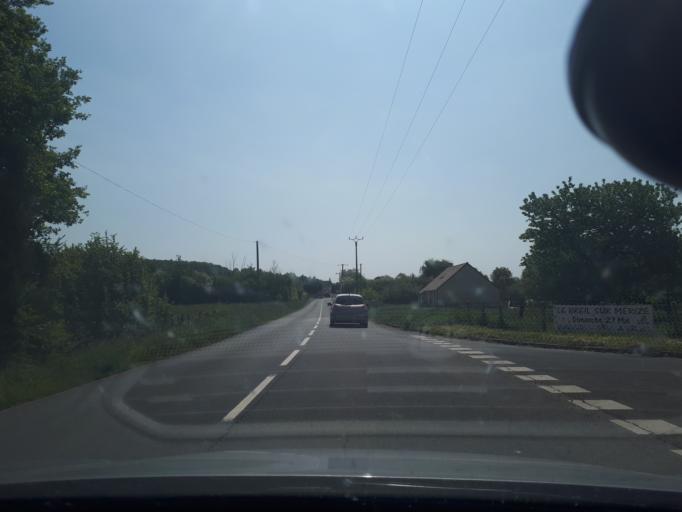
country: FR
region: Pays de la Loire
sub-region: Departement de la Sarthe
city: Le Breil-sur-Merize
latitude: 48.0124
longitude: 0.4721
